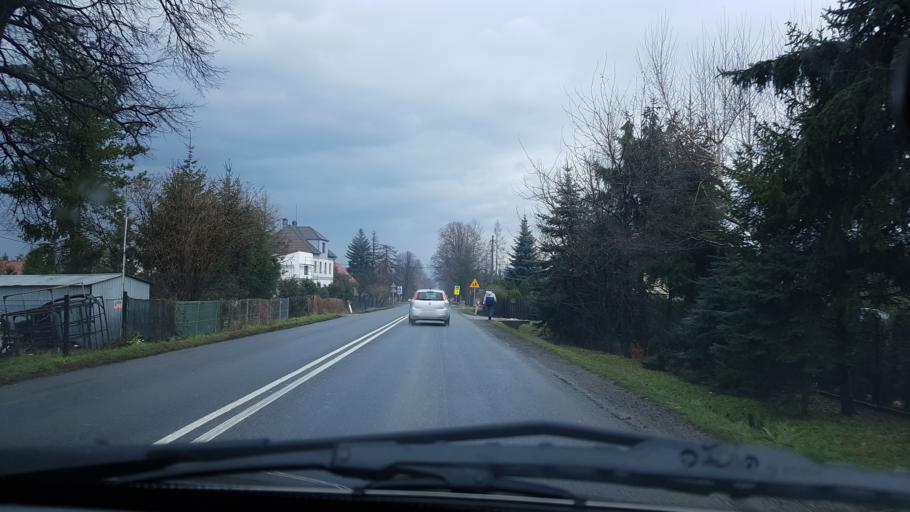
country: PL
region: Silesian Voivodeship
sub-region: Powiat zywiecki
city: Lodygowice
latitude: 49.7237
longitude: 19.1391
